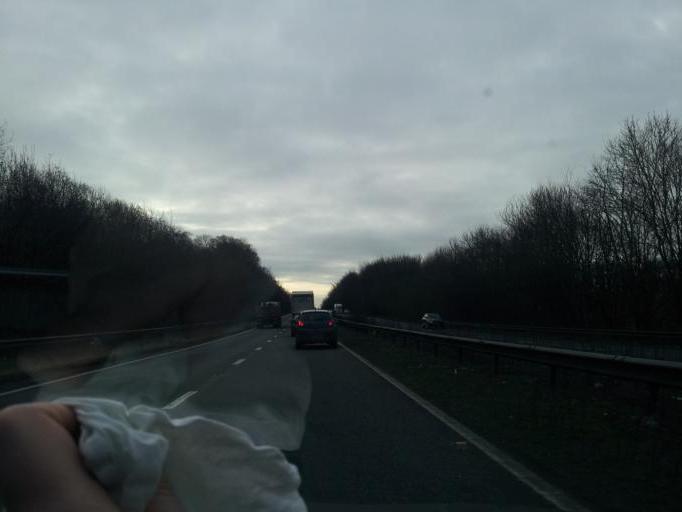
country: GB
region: England
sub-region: Lincolnshire
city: Grantham
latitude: 52.8241
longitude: -0.6284
